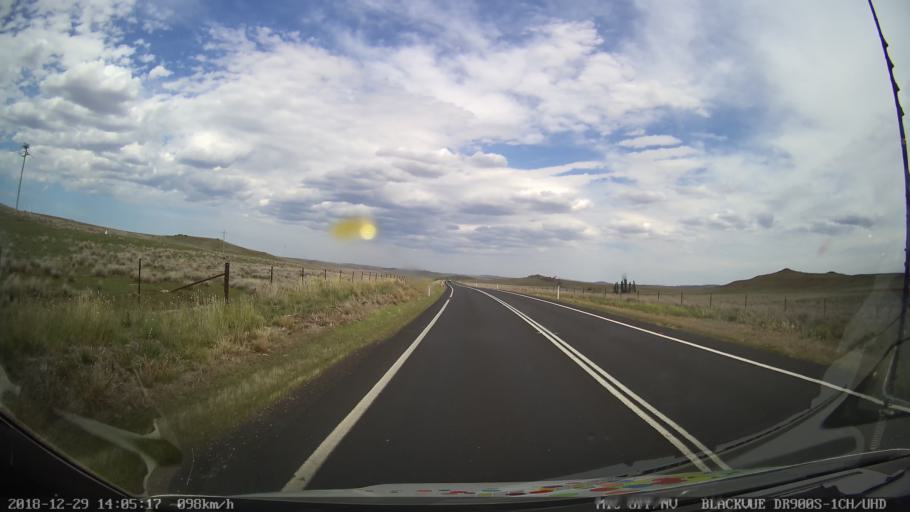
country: AU
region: New South Wales
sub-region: Cooma-Monaro
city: Cooma
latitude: -36.3284
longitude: 149.1906
